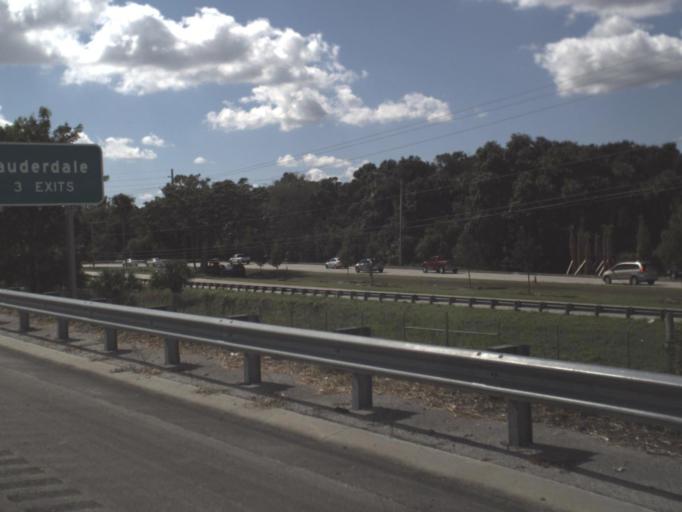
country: US
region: Florida
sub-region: Broward County
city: Palm Aire
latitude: 26.2216
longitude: -80.1865
